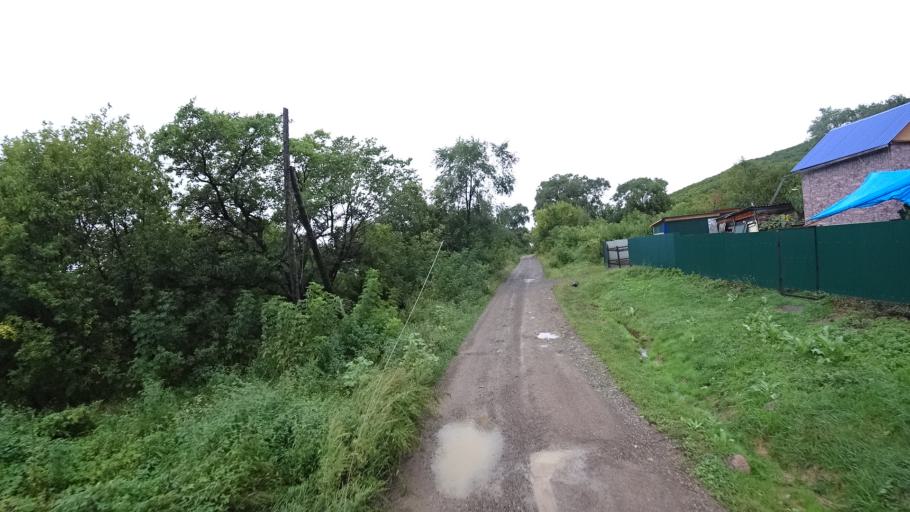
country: RU
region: Primorskiy
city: Monastyrishche
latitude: 44.2620
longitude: 132.4054
